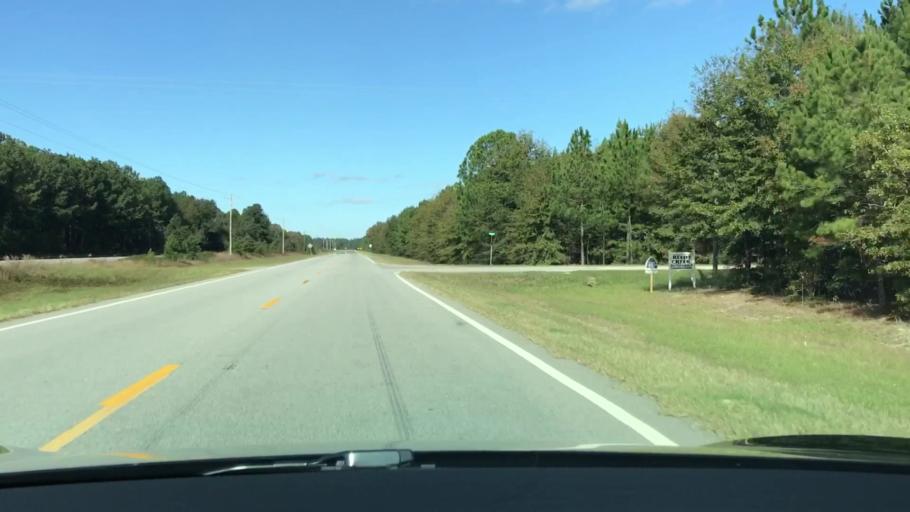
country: US
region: Georgia
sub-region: Glascock County
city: Gibson
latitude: 33.2977
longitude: -82.5155
